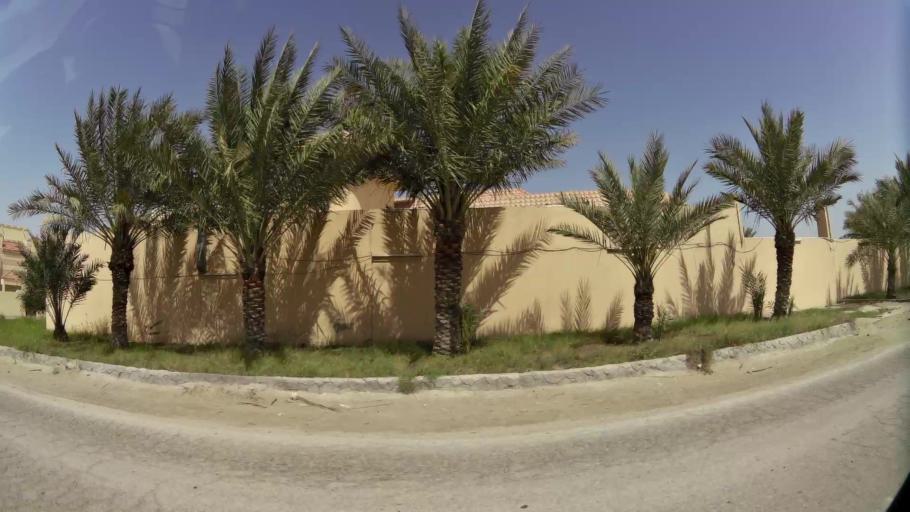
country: QA
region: Baladiyat Umm Salal
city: Umm Salal Muhammad
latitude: 25.3750
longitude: 51.4181
